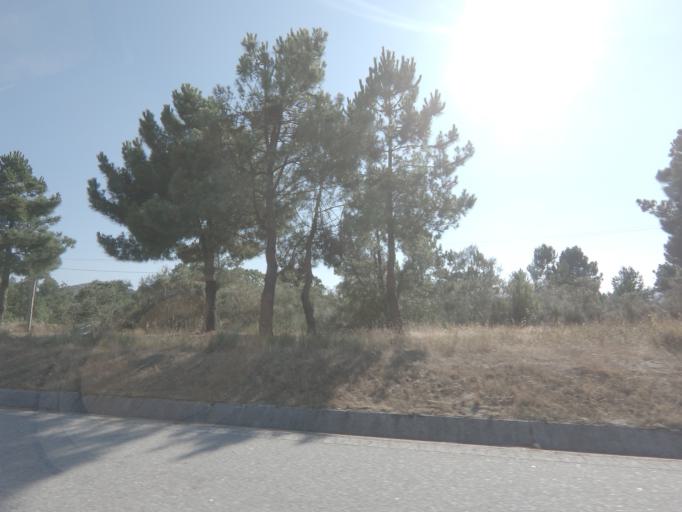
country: PT
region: Viseu
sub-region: Moimenta da Beira
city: Moimenta da Beira
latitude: 41.0384
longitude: -7.5694
